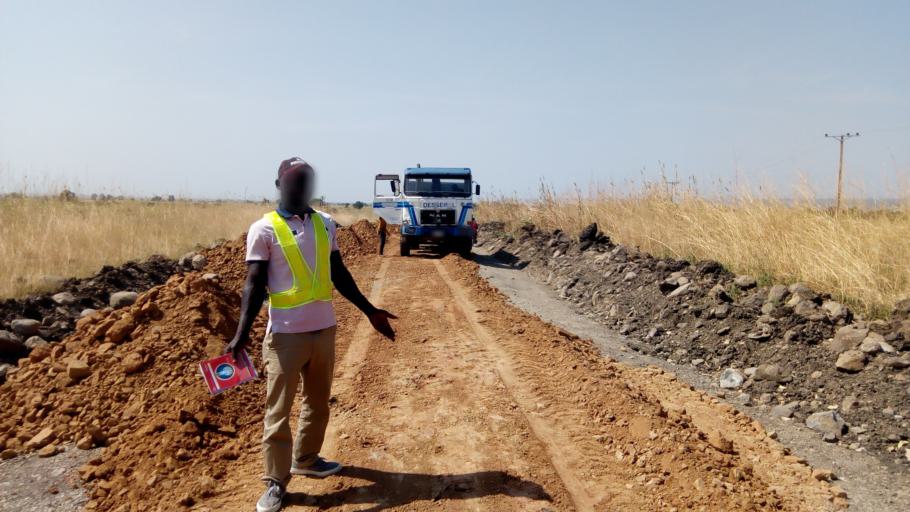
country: NG
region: Adamawa
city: Numan
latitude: 9.6888
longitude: 11.8782
